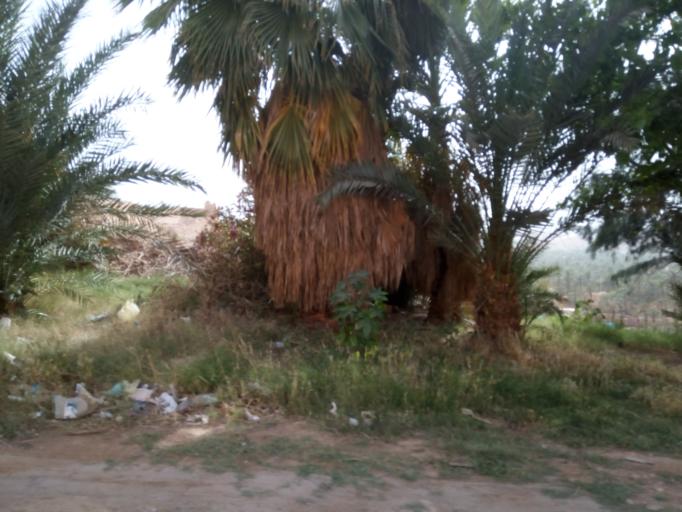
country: DZ
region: Ghardaia
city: Ghardaia
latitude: 32.4649
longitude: 3.6906
